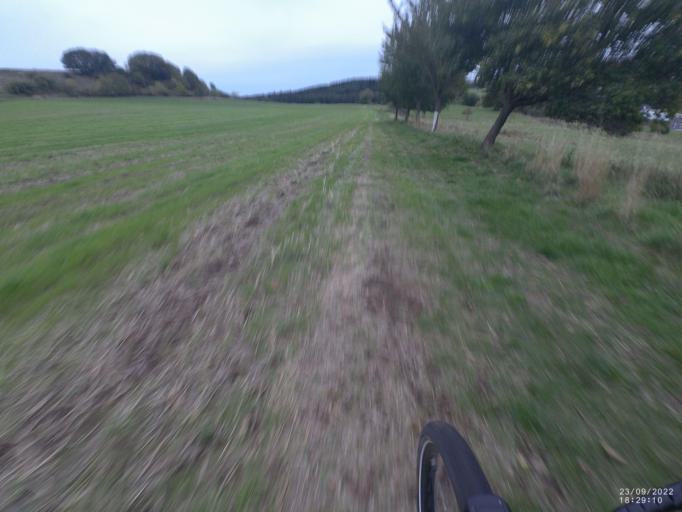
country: DE
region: Rheinland-Pfalz
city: Dockweiler
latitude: 50.2320
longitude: 6.7909
